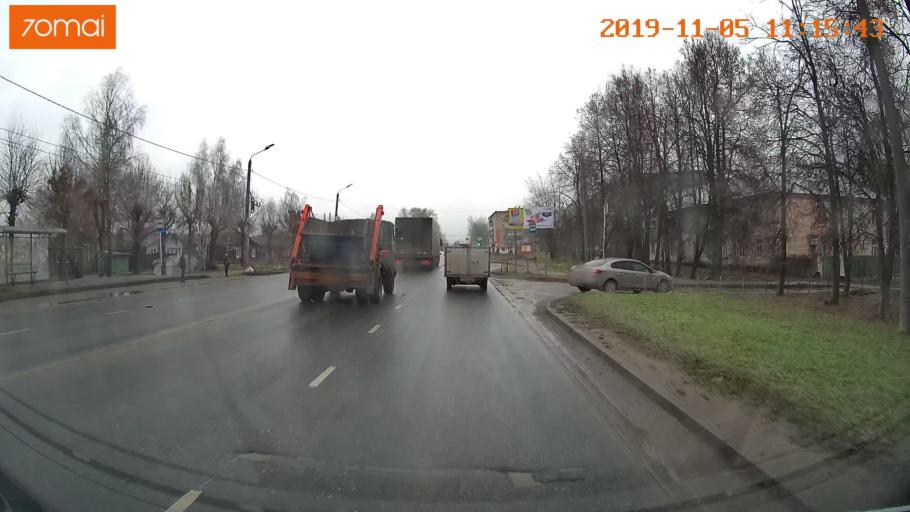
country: RU
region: Ivanovo
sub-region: Gorod Ivanovo
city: Ivanovo
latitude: 56.9793
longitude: 40.9540
